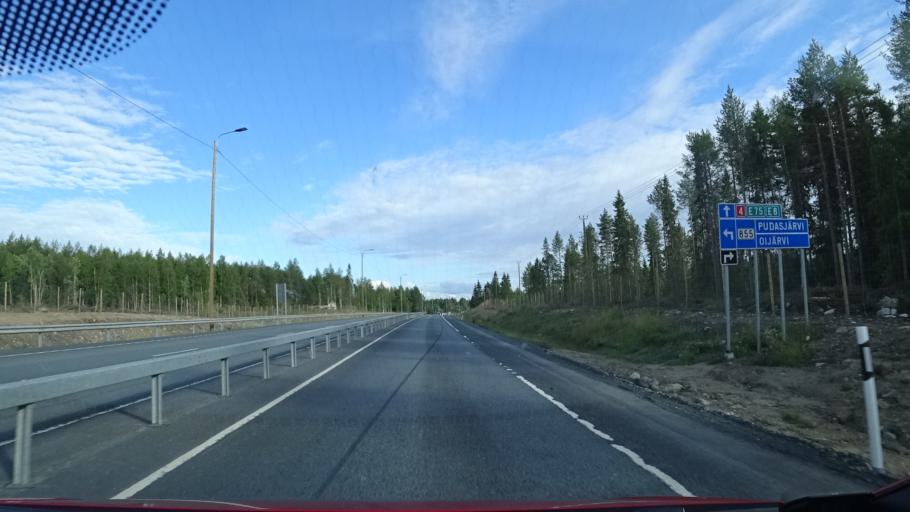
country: FI
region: Northern Ostrobothnia
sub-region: Oulunkaari
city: Ii
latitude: 65.4687
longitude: 25.3671
